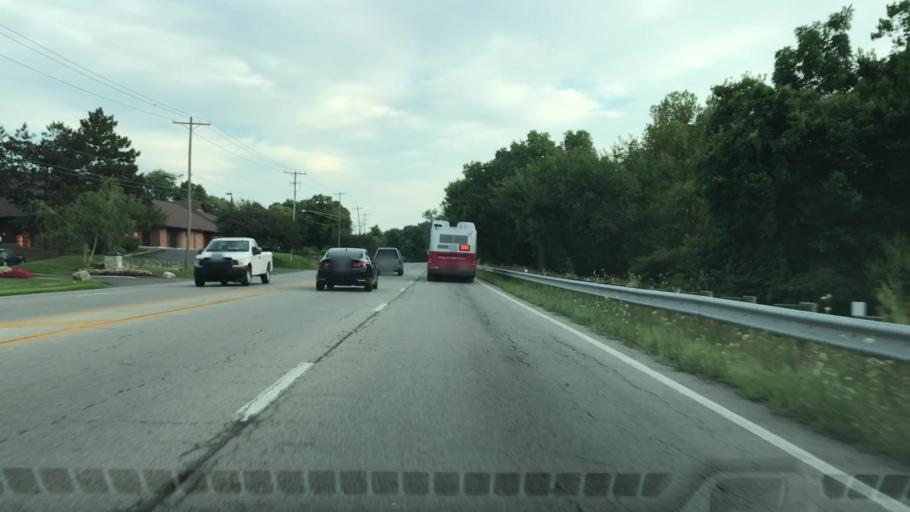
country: US
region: Ohio
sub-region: Franklin County
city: Upper Arlington
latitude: 40.0243
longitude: -83.0917
